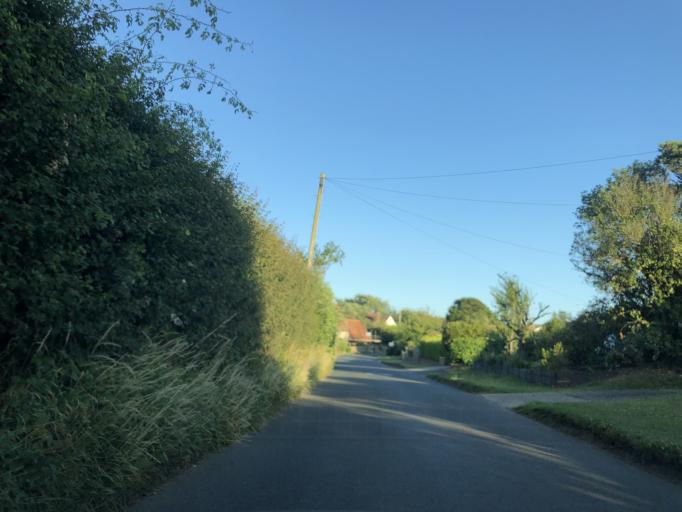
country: GB
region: England
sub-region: Isle of Wight
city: Chale
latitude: 50.6431
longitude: -1.3540
